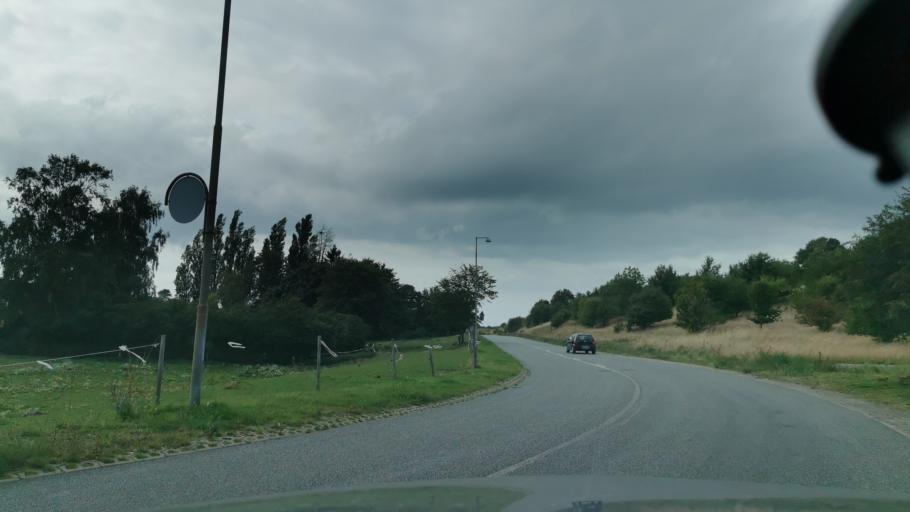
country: DK
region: Zealand
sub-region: Kalundborg Kommune
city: Kalundborg
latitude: 55.6951
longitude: 11.0645
